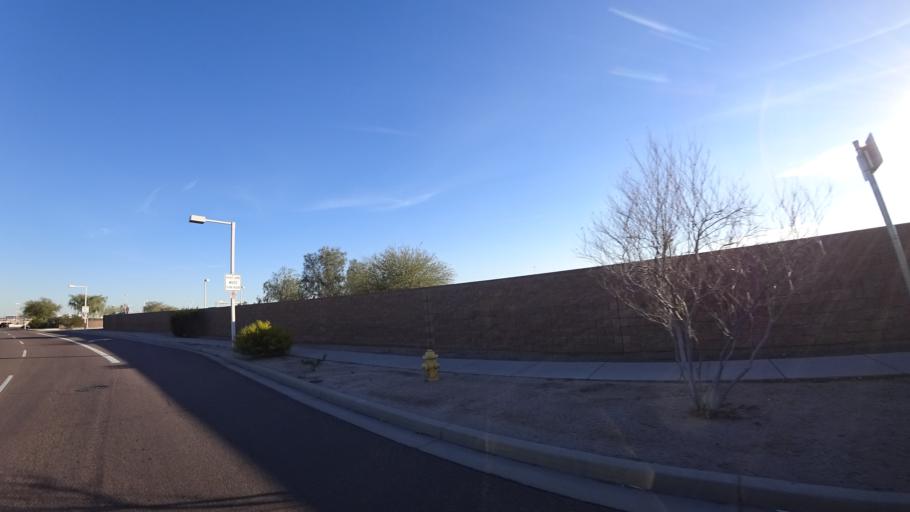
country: US
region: Arizona
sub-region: Maricopa County
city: Phoenix
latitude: 33.4295
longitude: -112.0335
